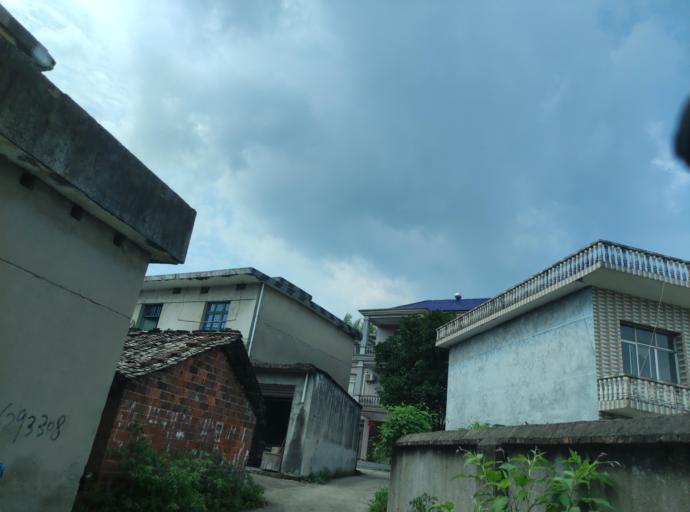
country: CN
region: Jiangxi Sheng
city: Yuannan
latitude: 27.6686
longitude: 114.0417
